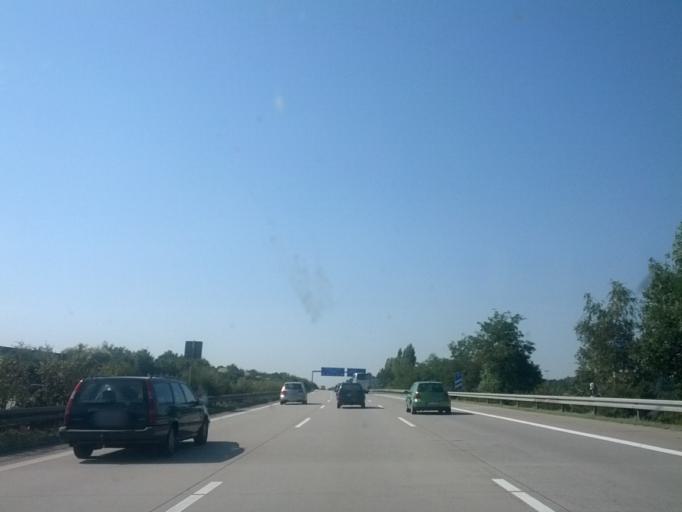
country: DE
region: Brandenburg
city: Linthe
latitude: 52.1612
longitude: 12.7849
